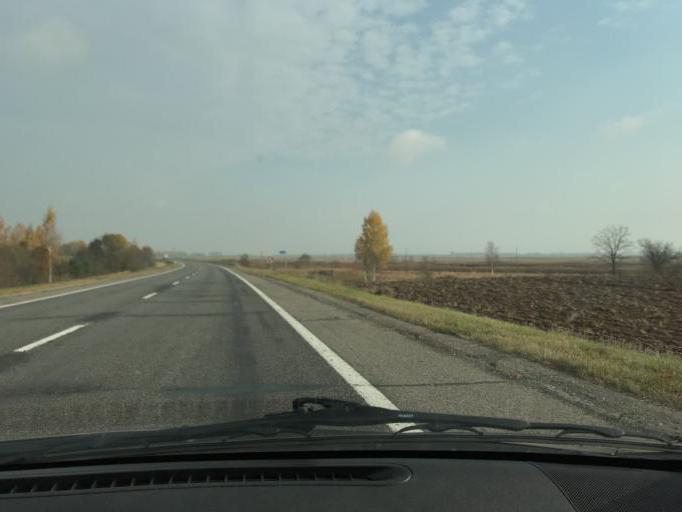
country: BY
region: Vitebsk
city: Chashniki
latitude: 54.9978
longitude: 28.9552
